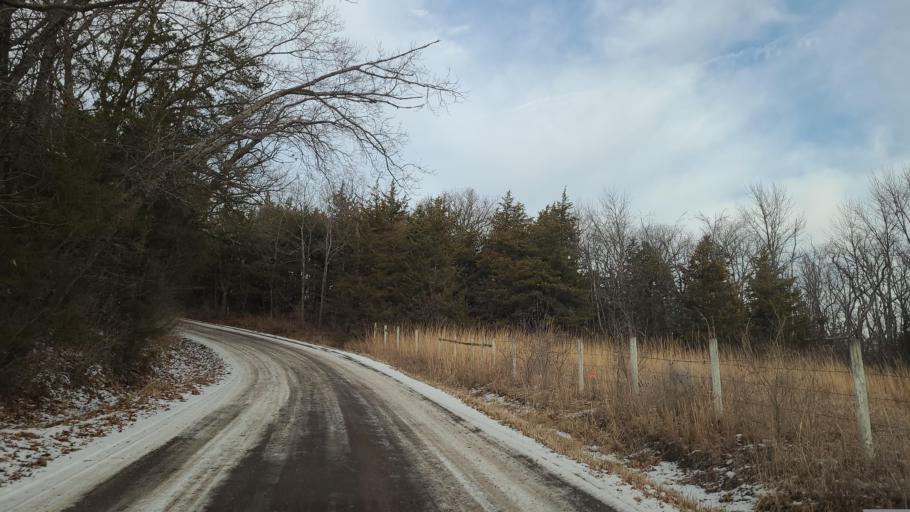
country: US
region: Kansas
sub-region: Shawnee County
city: Topeka
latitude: 39.0518
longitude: -95.4941
